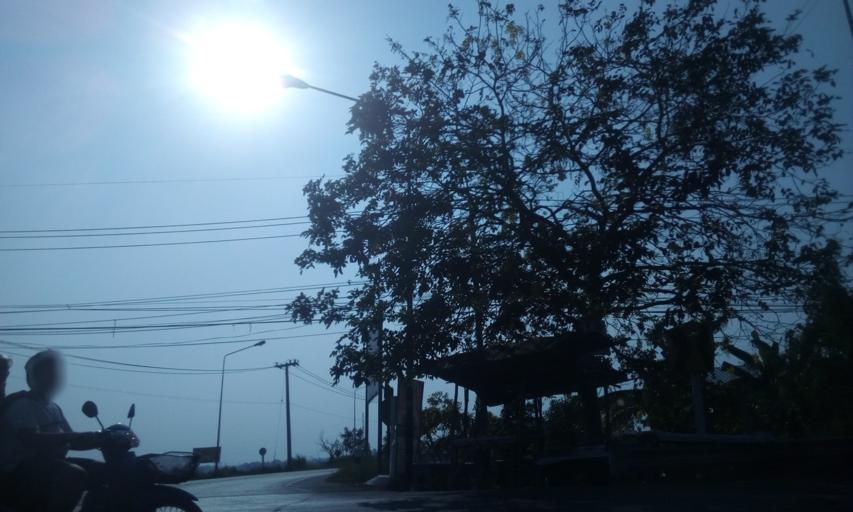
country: TH
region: Sing Buri
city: Phrom Buri
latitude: 14.7791
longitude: 100.4341
